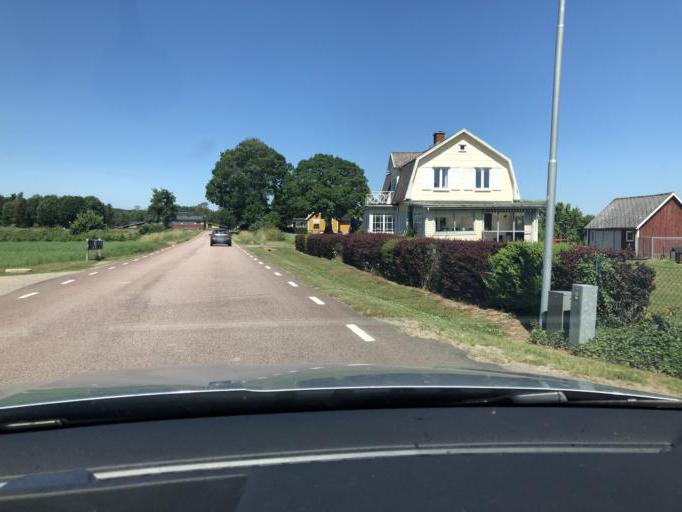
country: SE
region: Blekinge
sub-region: Olofstroms Kommun
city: Jamshog
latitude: 56.1802
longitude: 14.6124
